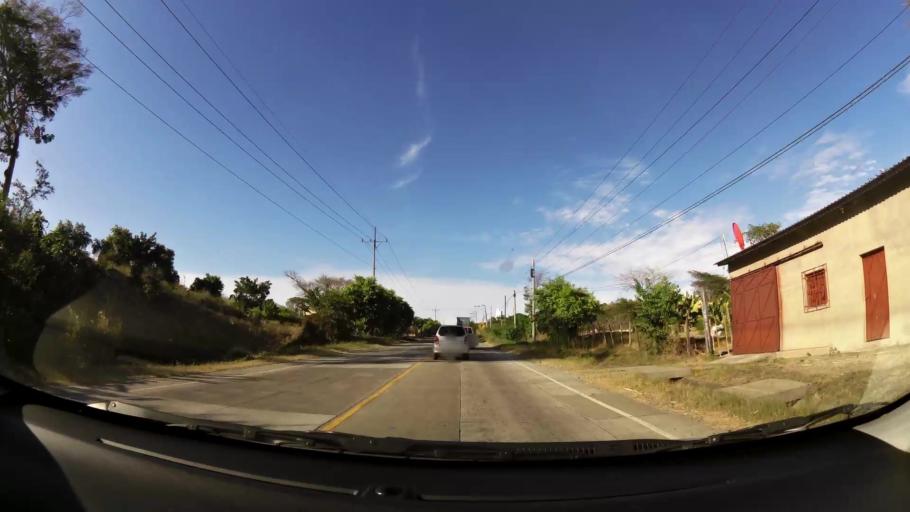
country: SV
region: Santa Ana
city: Metapan
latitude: 14.2868
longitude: -89.4620
